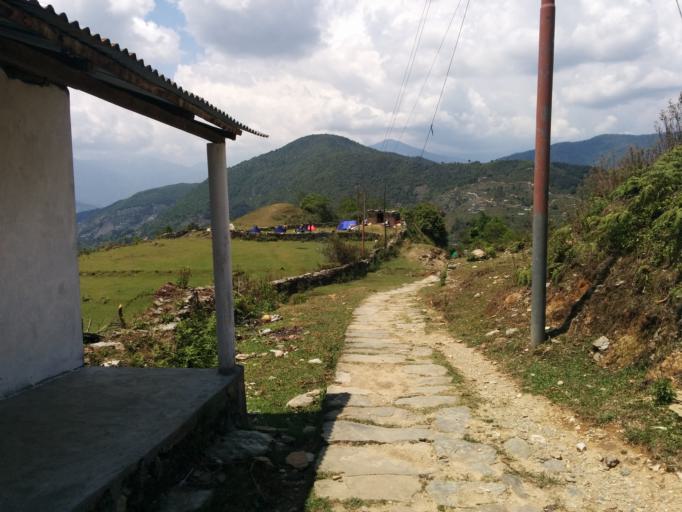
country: NP
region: Western Region
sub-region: Gandaki Zone
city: Pokhara
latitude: 28.2594
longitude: 83.8209
